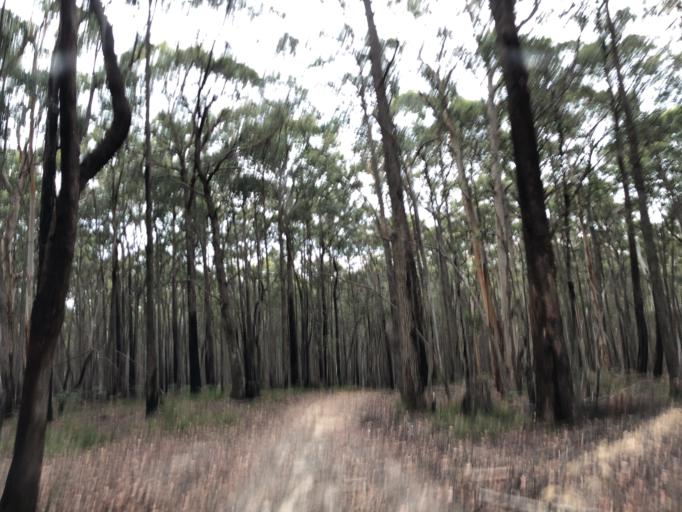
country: AU
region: Victoria
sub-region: Moorabool
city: Bacchus Marsh
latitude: -37.4431
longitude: 144.3347
